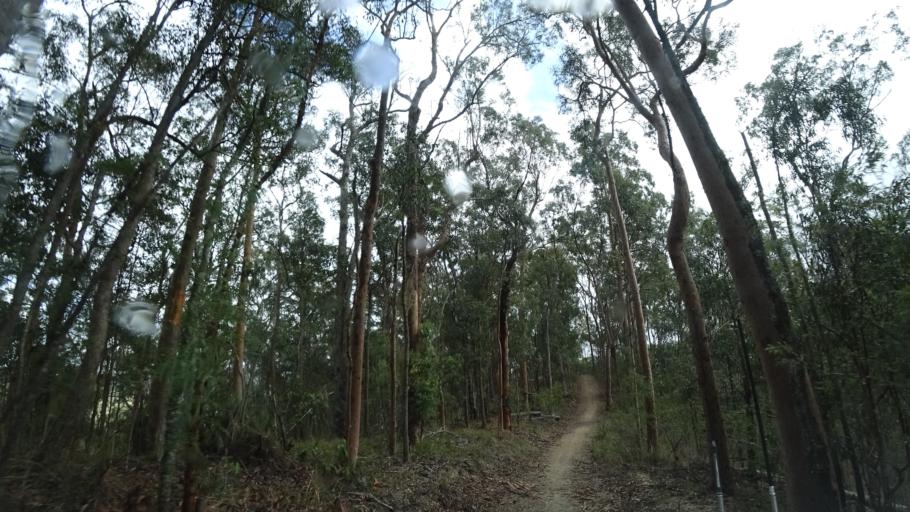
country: AU
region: Queensland
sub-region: Brisbane
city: Pullenvale
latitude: -27.4607
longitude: 152.8349
